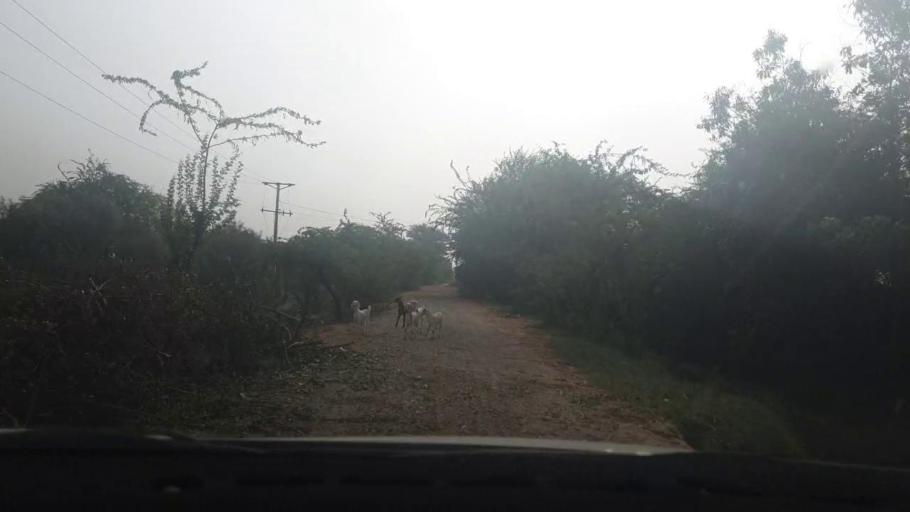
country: PK
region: Sindh
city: Tando Muhammad Khan
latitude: 25.1028
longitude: 68.5371
